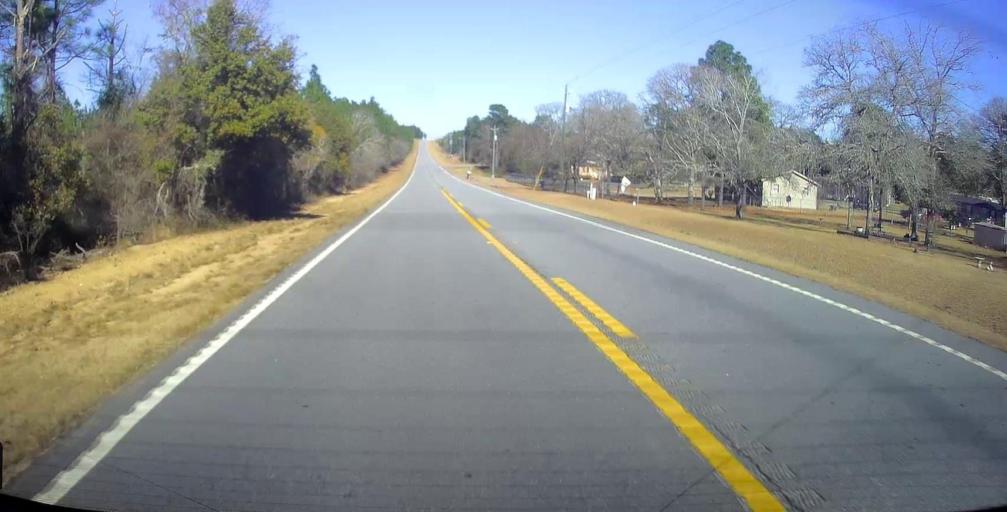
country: US
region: Georgia
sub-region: Taylor County
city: Butler
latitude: 32.5739
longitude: -84.2166
